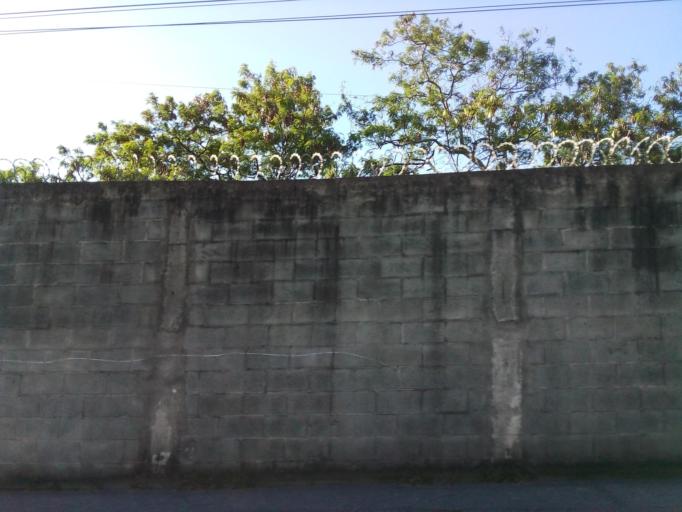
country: BR
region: Espirito Santo
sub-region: Vitoria
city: Vitoria
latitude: -20.3261
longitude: -40.3436
